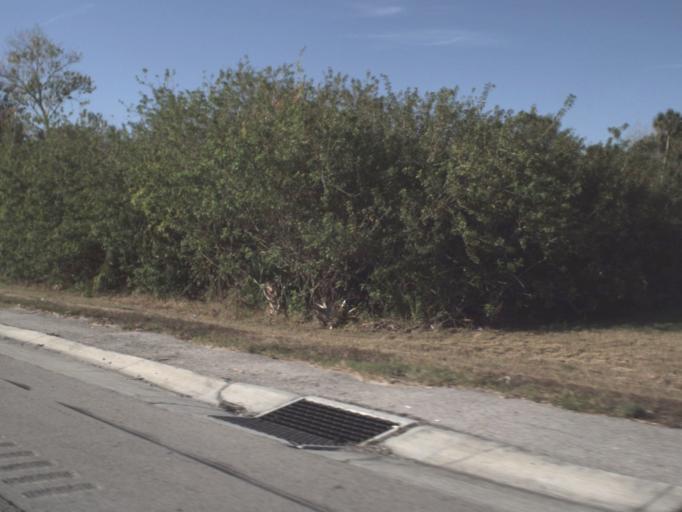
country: US
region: Florida
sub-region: Brevard County
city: West Melbourne
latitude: 28.0253
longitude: -80.6493
